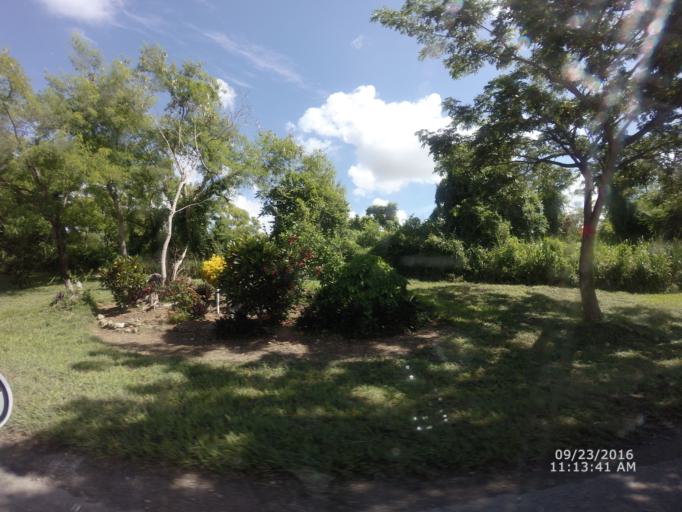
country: CU
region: La Habana
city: Arroyo Naranjo
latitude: 23.0311
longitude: -82.2993
